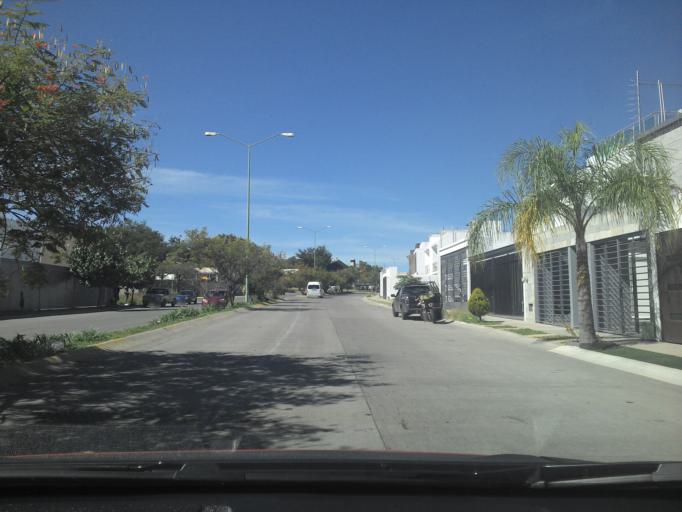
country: MX
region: Jalisco
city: Nuevo Mexico
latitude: 20.7488
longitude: -103.4119
